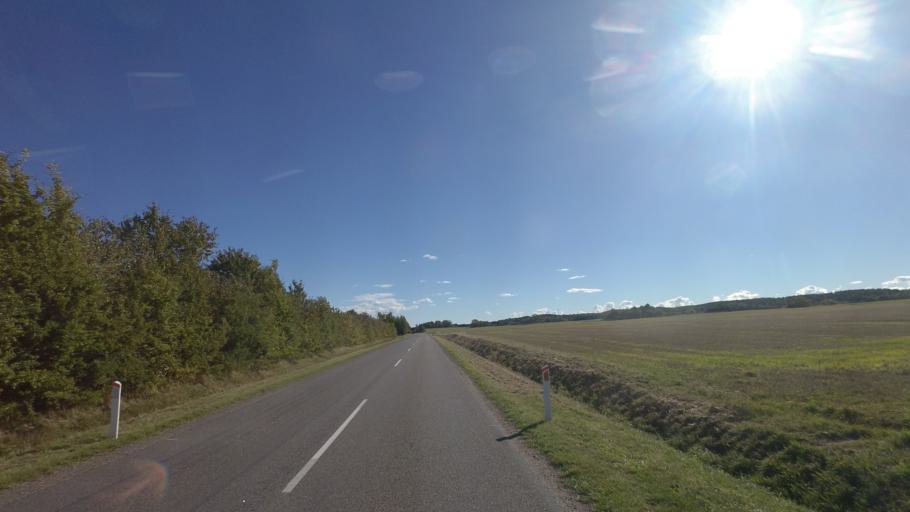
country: DK
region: Capital Region
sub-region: Bornholm Kommune
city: Nexo
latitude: 55.1110
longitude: 15.1105
